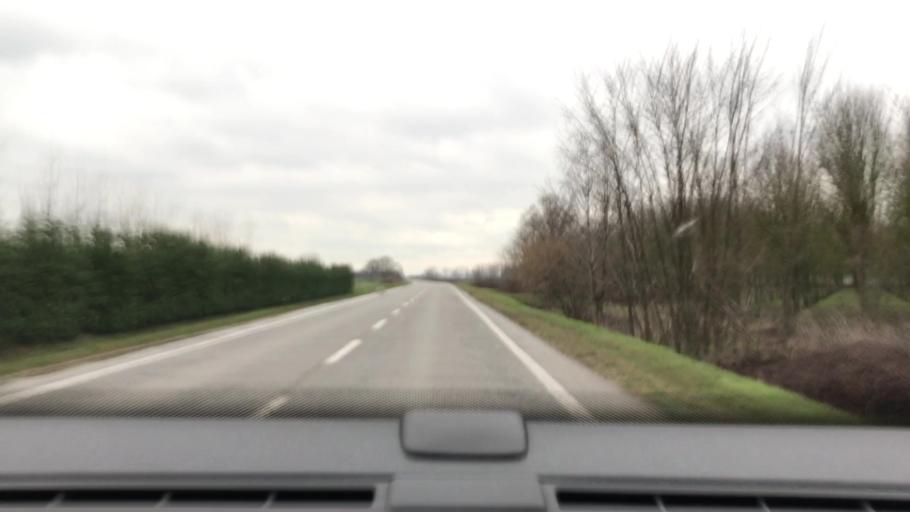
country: IT
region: Lombardy
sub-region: Provincia di Cremona
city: Torricella del Pizzo
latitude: 45.0362
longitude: 10.2982
